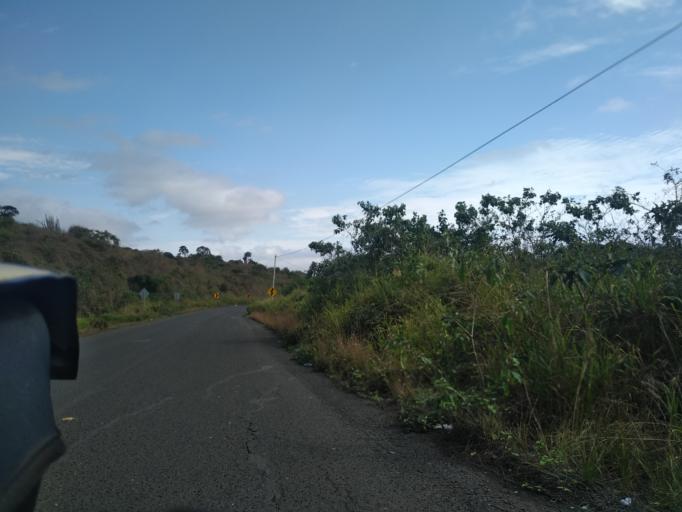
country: EC
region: Manabi
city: Jipijapa
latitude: -1.4408
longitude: -80.7532
